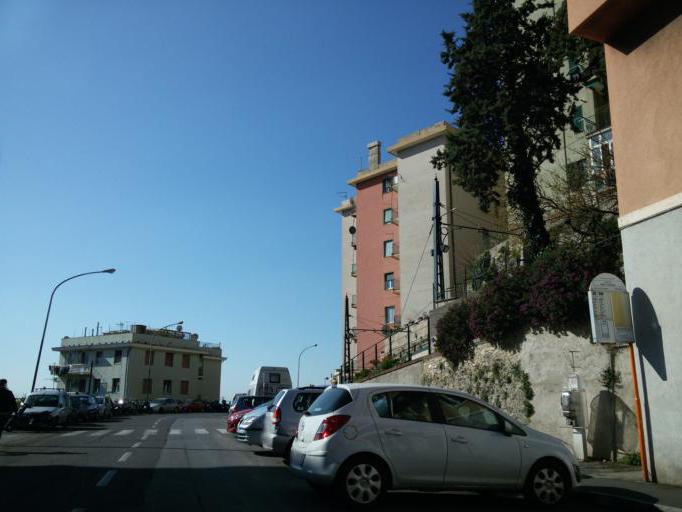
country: IT
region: Liguria
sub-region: Provincia di Genova
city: Genoa
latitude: 44.4213
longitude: 8.9168
